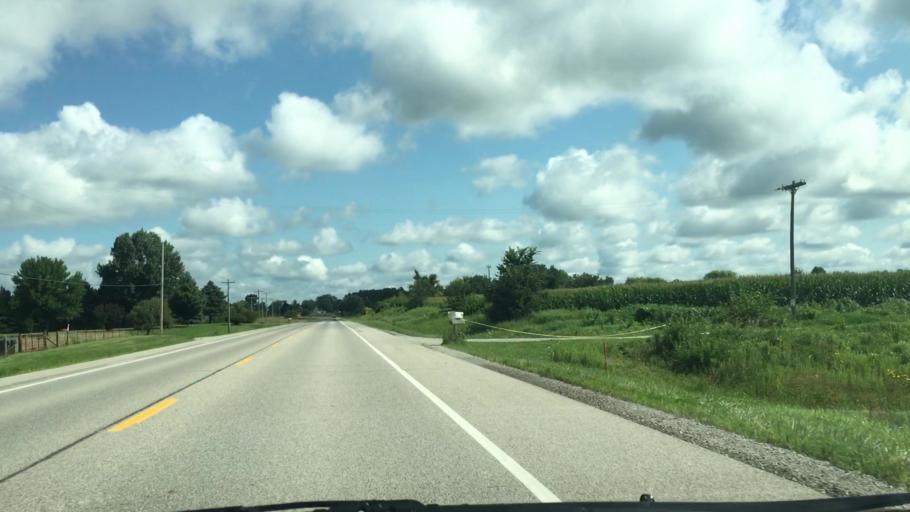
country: US
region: Iowa
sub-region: Johnson County
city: Solon
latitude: 41.7306
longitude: -91.4757
